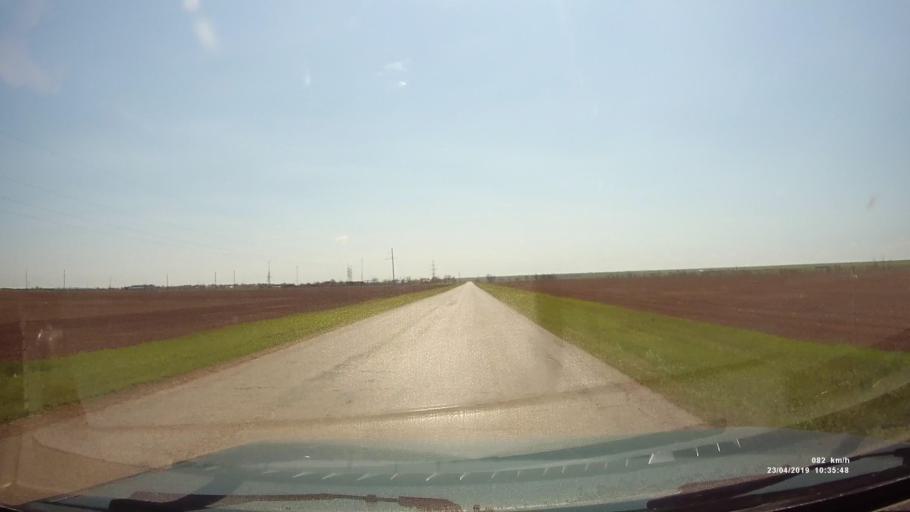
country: RU
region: Kalmykiya
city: Yashalta
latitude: 46.5505
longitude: 42.6287
